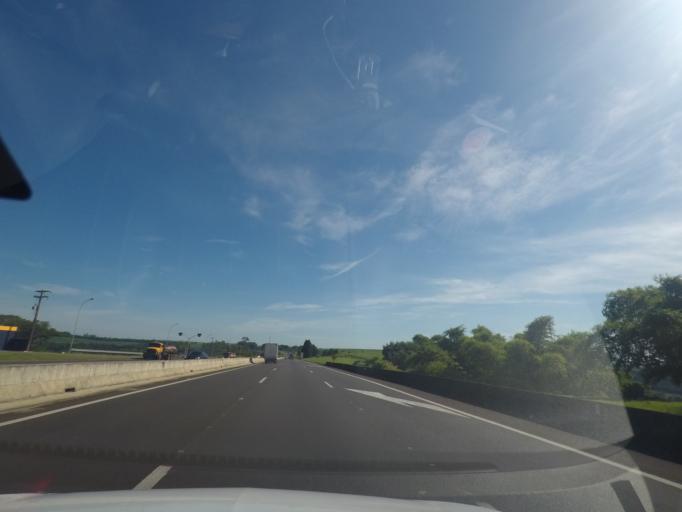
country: BR
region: Sao Paulo
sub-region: Itirapina
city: Itirapina
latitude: -22.2669
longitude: -47.7039
